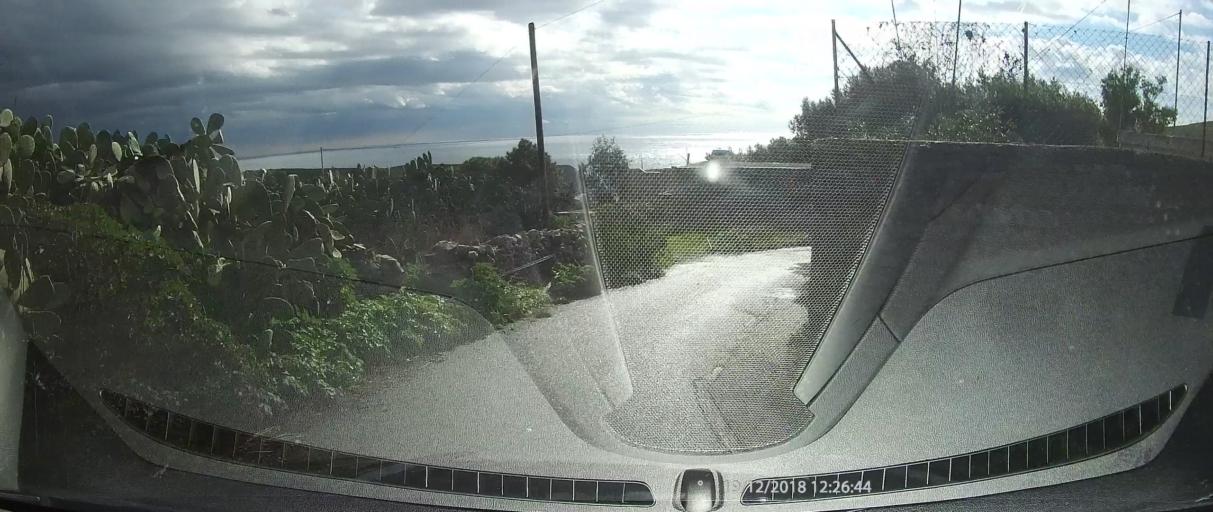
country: GR
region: Peloponnese
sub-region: Nomos Lakonias
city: Gytheio
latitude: 36.4042
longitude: 22.4869
